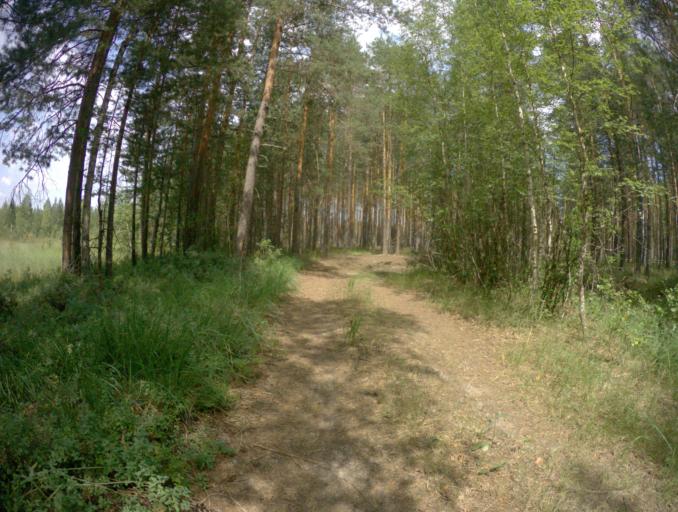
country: RU
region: Ivanovo
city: Talitsy
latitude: 56.3903
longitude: 42.3475
